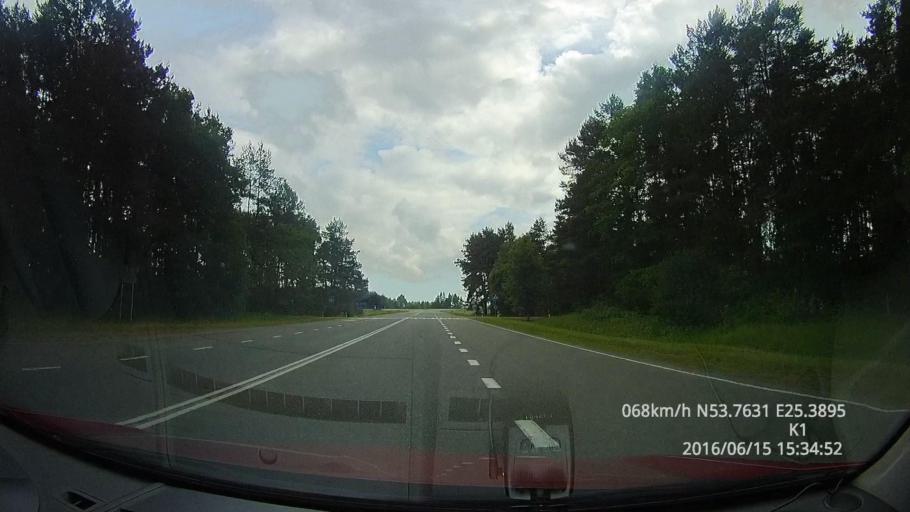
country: BY
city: Berezovka
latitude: 53.7626
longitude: 25.3898
